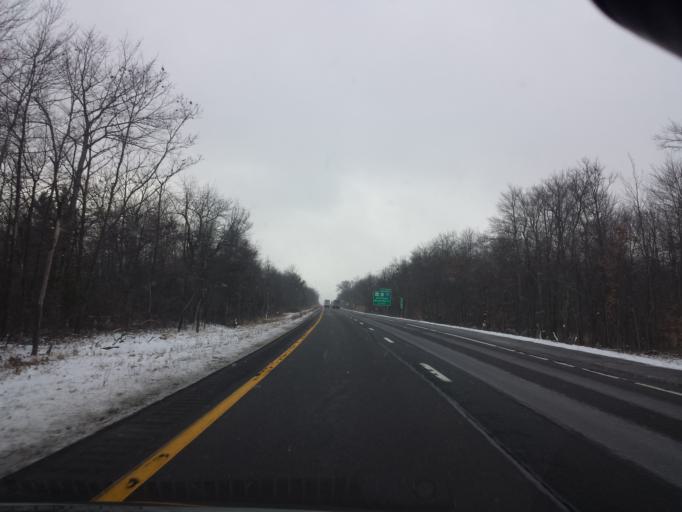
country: US
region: Pennsylvania
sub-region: Carbon County
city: Towamensing Trails
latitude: 41.0799
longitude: -75.6634
